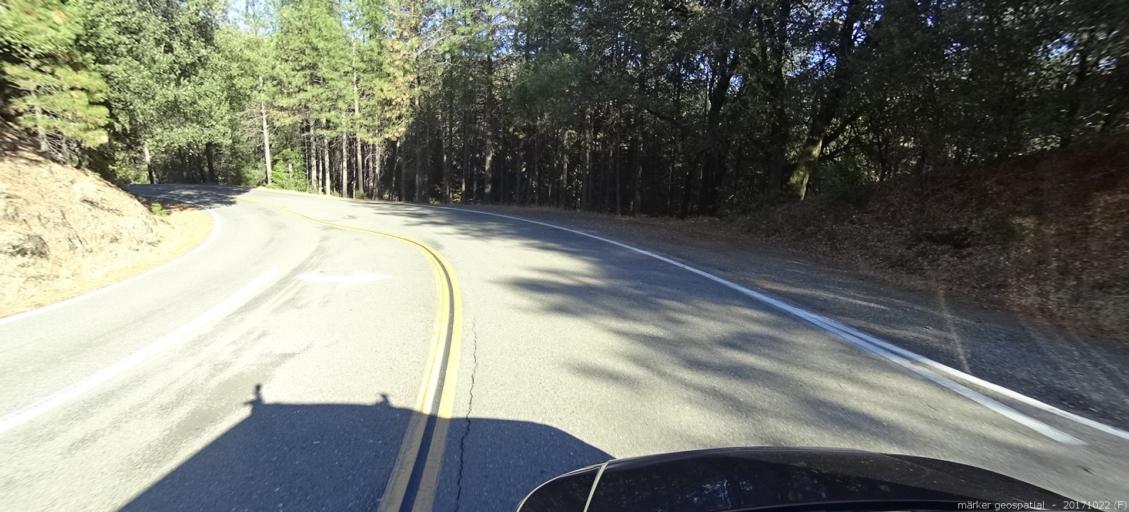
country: US
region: California
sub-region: Shasta County
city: Shasta Lake
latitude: 40.8732
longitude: -122.2485
